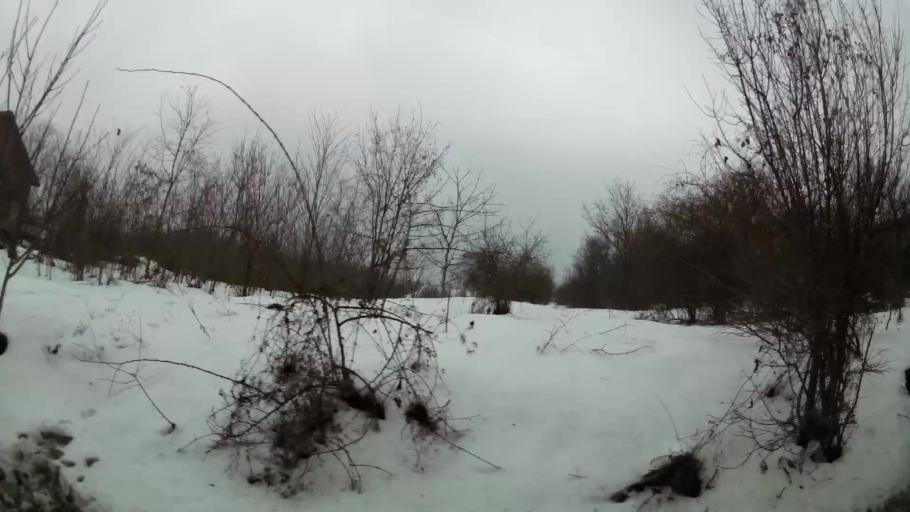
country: RS
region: Central Serbia
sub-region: Belgrade
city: Zvezdara
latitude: 44.7497
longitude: 20.5262
